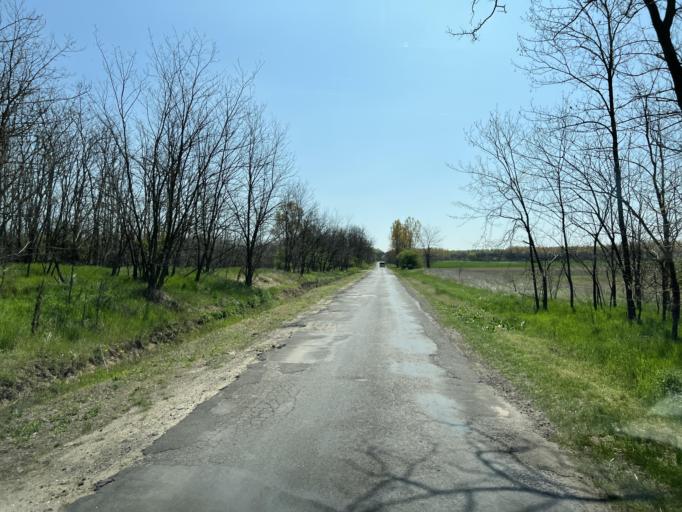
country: HU
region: Pest
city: Ujhartyan
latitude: 47.1733
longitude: 19.3711
